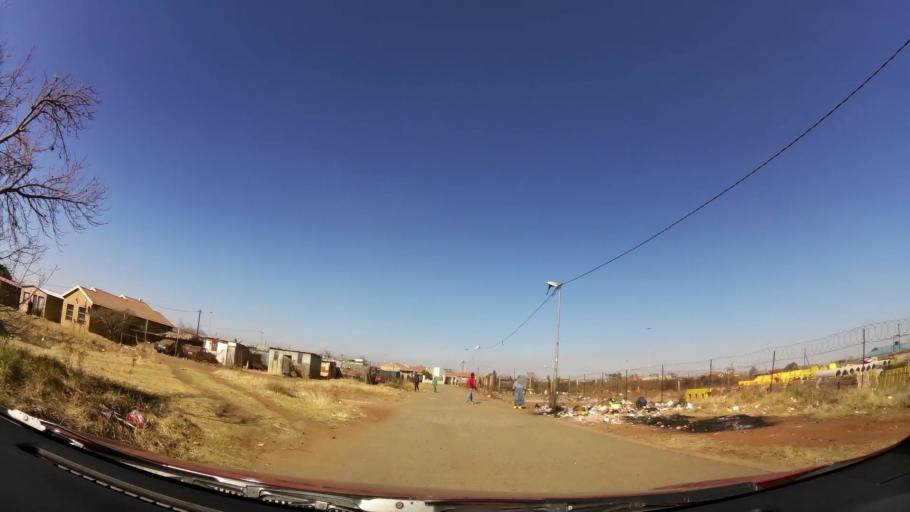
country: ZA
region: Gauteng
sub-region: City of Johannesburg Metropolitan Municipality
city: Soweto
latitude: -26.2161
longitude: 27.8295
